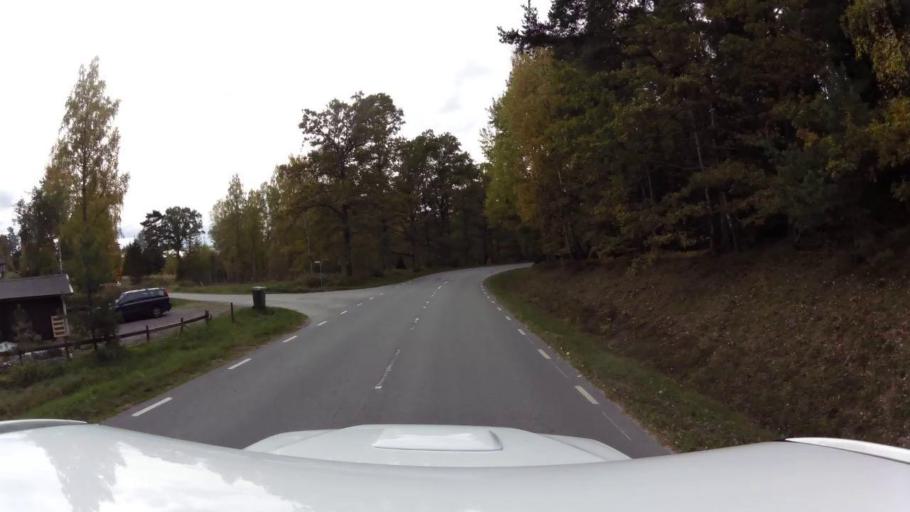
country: SE
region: OEstergoetland
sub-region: Linkopings Kommun
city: Ekangen
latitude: 58.5414
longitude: 15.6340
